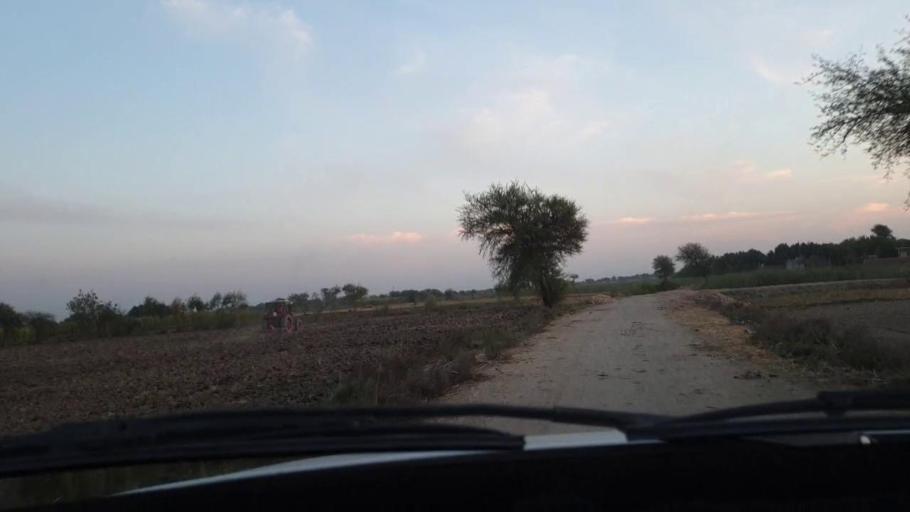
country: PK
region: Sindh
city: Tando Muhammad Khan
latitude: 25.0808
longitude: 68.3988
